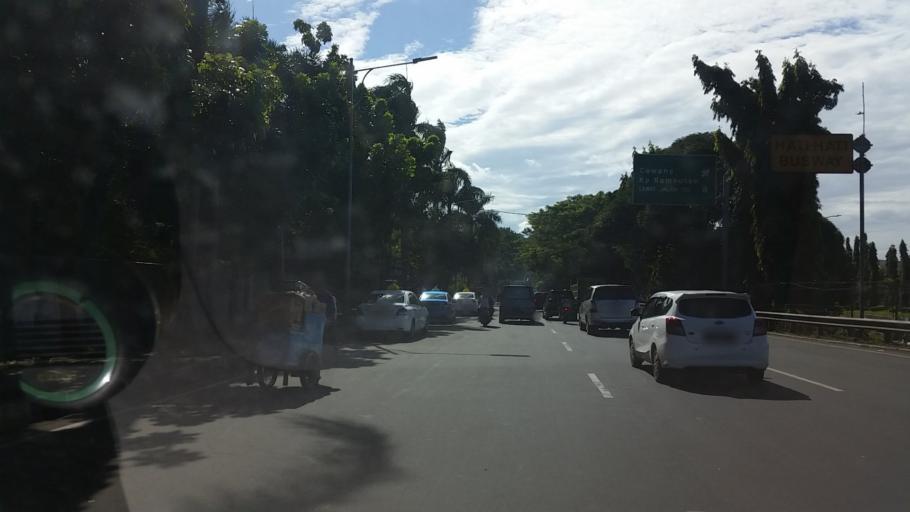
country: ID
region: Banten
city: South Tangerang
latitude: -6.2819
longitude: 106.7729
